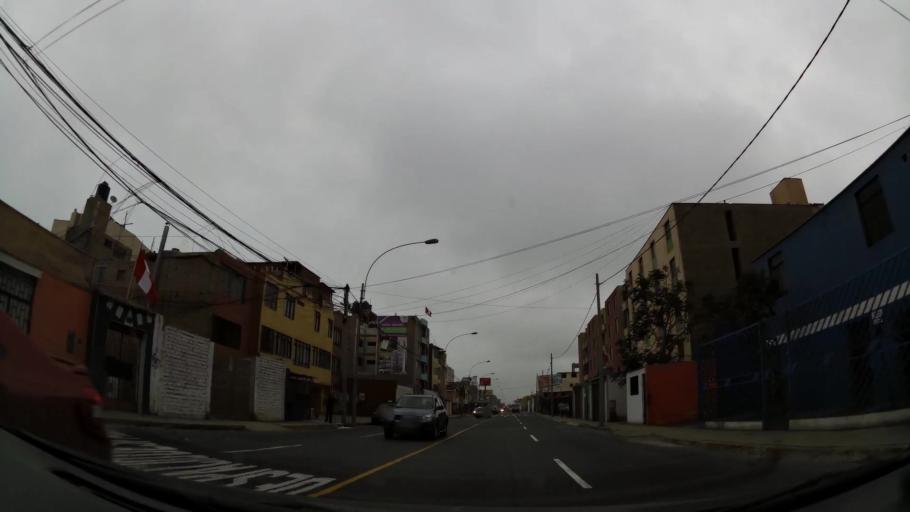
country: PE
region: Callao
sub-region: Callao
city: Callao
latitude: -12.0805
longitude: -77.1047
